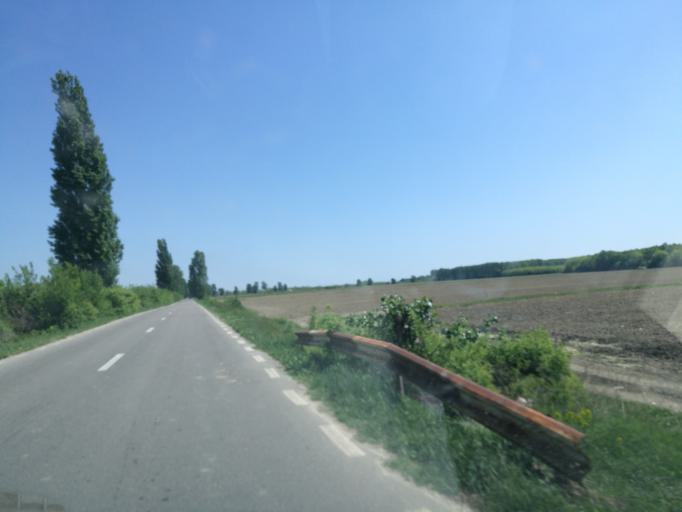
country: RO
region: Ialomita
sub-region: Comuna Adancata
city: Adancata
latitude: 44.7549
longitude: 26.4296
